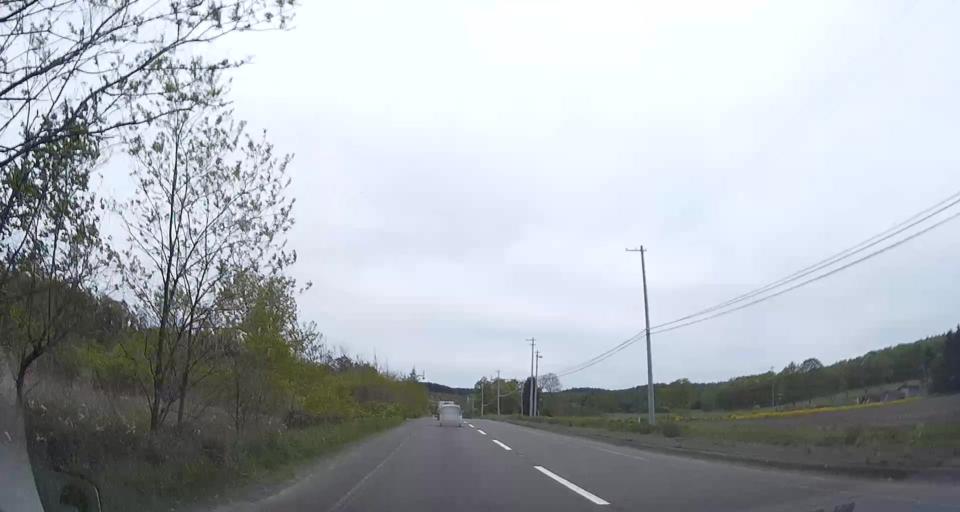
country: JP
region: Hokkaido
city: Chitose
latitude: 42.7706
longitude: 141.8373
